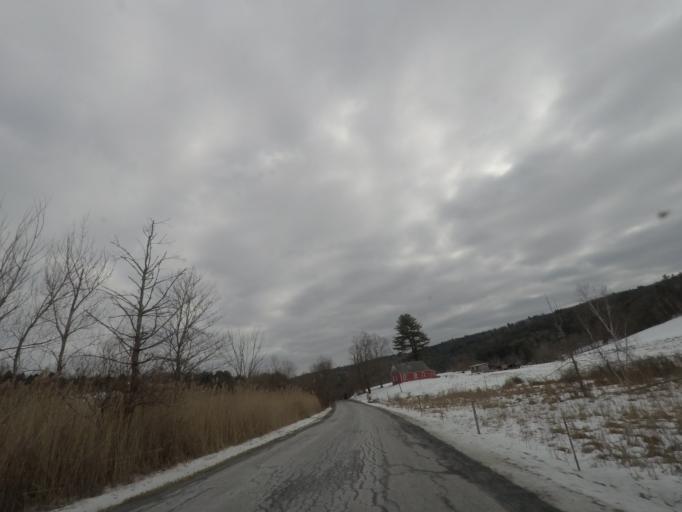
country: US
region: New York
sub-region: Rensselaer County
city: Hoosick Falls
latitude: 42.8691
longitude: -73.3893
